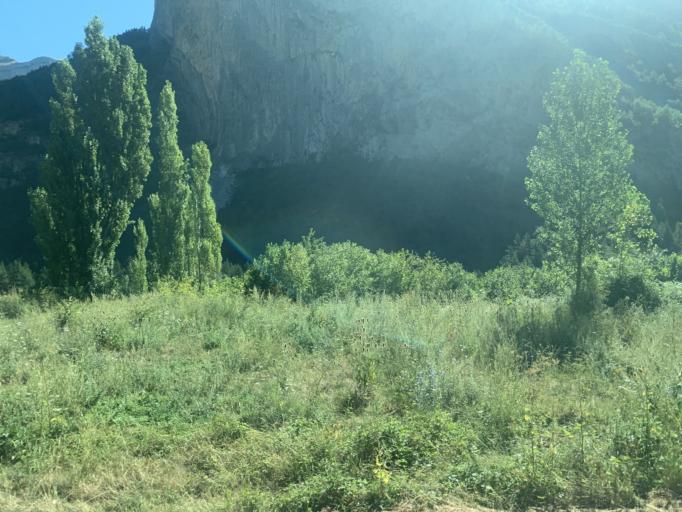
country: ES
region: Aragon
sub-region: Provincia de Huesca
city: Broto
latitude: 42.6434
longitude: -0.1077
